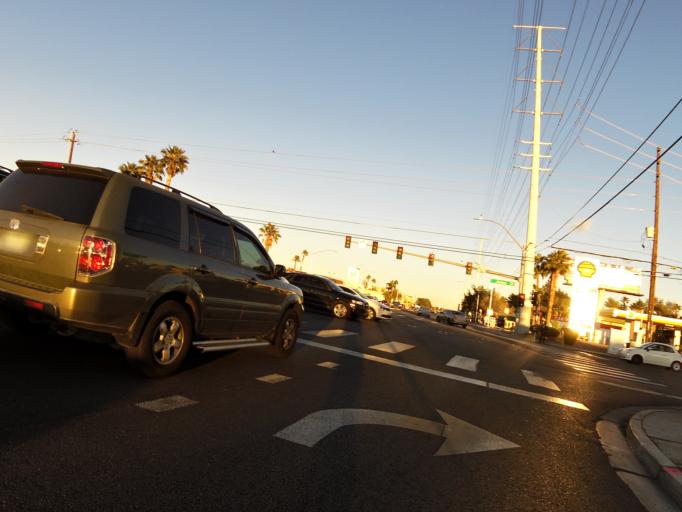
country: US
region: Nevada
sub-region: Clark County
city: Spring Valley
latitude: 36.1144
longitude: -115.2252
